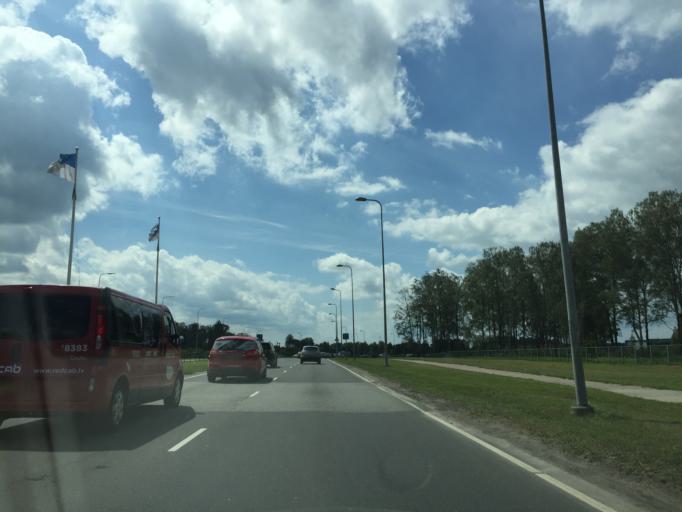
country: LV
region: Marupe
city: Marupe
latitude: 56.9295
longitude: 24.0322
